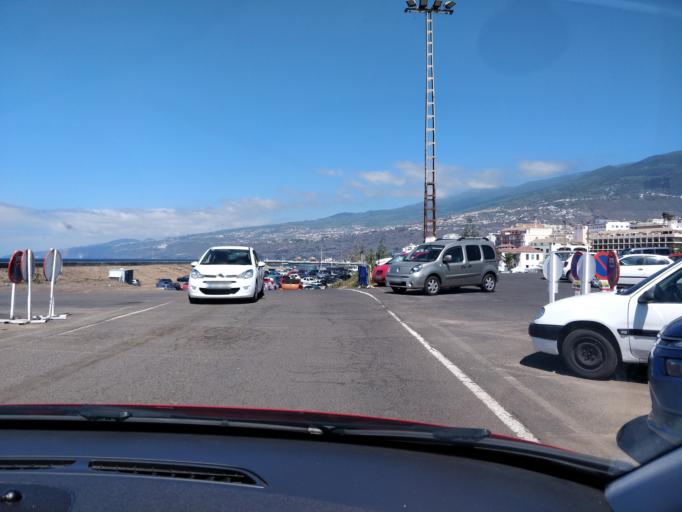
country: ES
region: Canary Islands
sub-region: Provincia de Santa Cruz de Tenerife
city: Puerto de la Cruz
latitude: 28.4184
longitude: -16.5529
